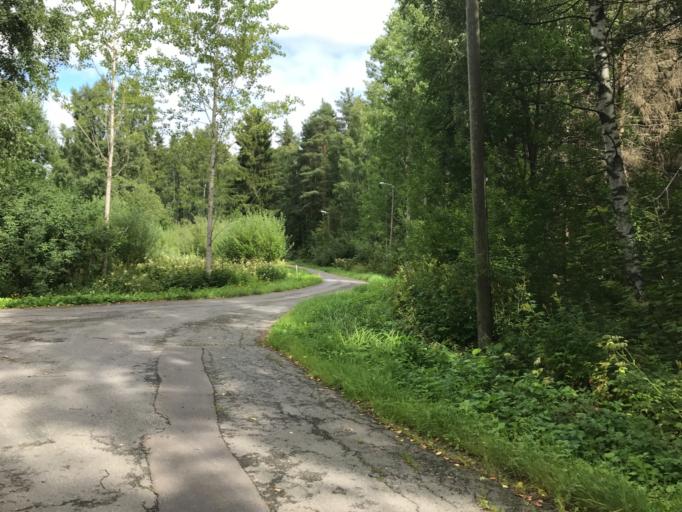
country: FI
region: Pirkanmaa
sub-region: Etelae-Pirkanmaa
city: Valkeakoski
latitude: 61.2559
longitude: 24.0441
